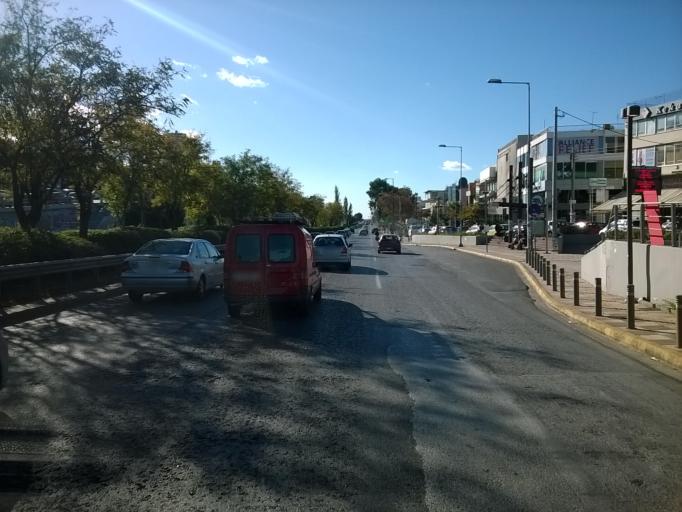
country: GR
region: Attica
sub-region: Nomarchia Athinas
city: Agios Dimitrios
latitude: 37.9296
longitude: 23.7443
